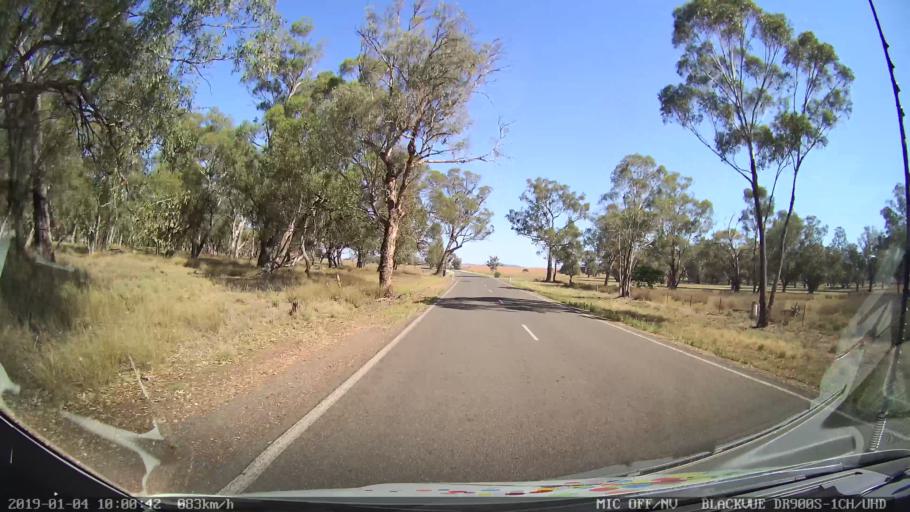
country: AU
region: New South Wales
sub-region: Cabonne
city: Canowindra
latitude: -33.4947
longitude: 148.3772
